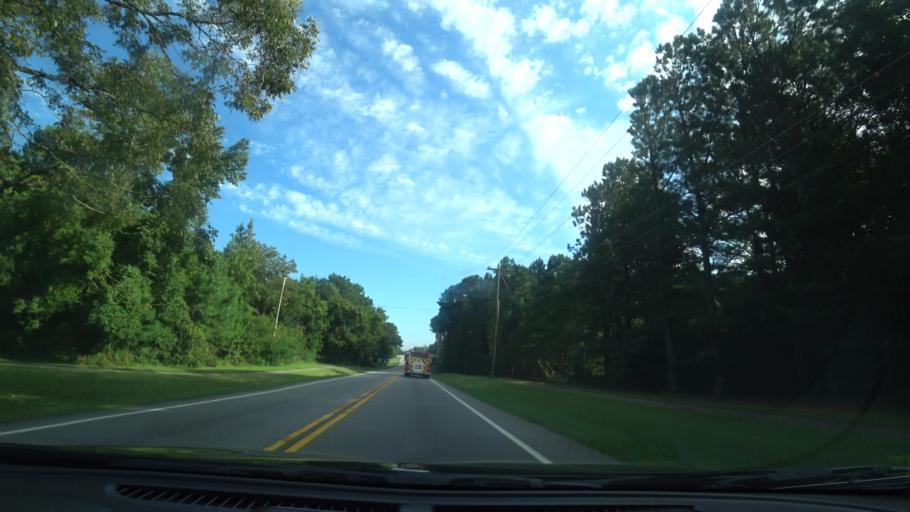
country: US
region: Georgia
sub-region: Gwinnett County
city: Grayson
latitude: 33.8412
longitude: -83.9589
